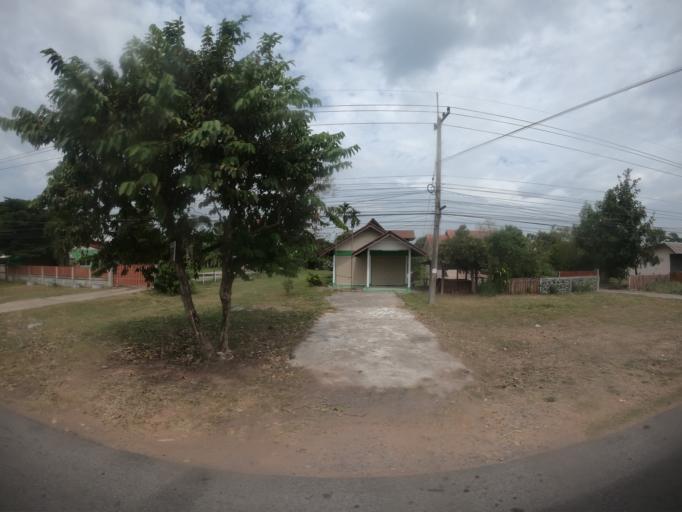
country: TH
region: Maha Sarakham
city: Maha Sarakham
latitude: 16.1603
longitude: 103.3552
